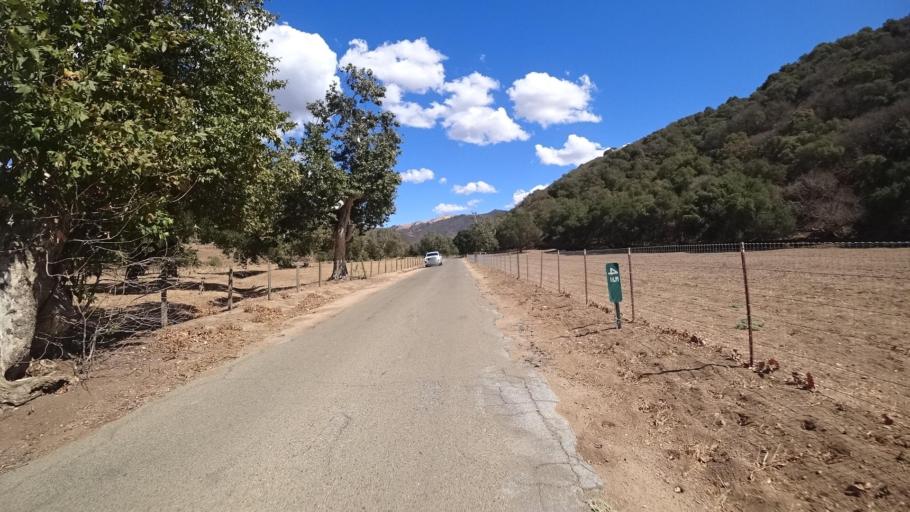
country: US
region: California
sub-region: Monterey County
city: Gonzales
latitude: 36.6030
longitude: -121.4239
